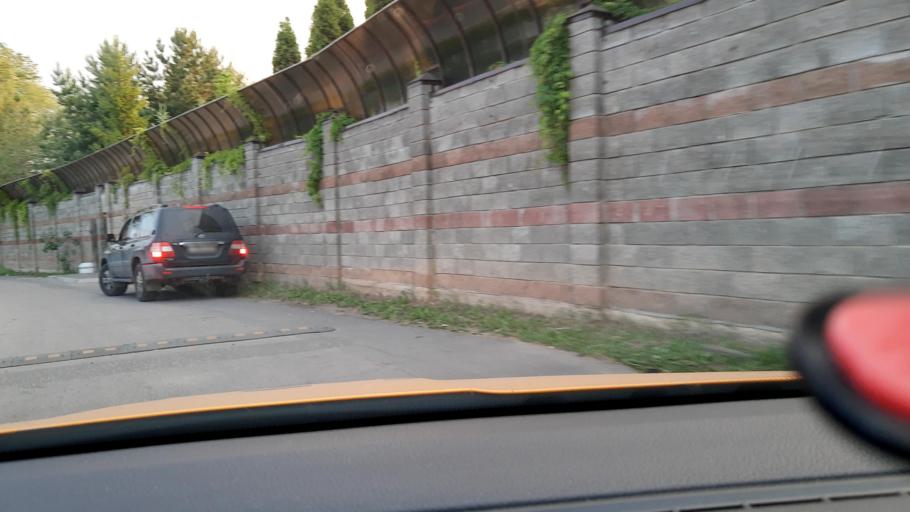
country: RU
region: Moskovskaya
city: Barvikha
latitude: 55.7281
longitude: 37.2922
